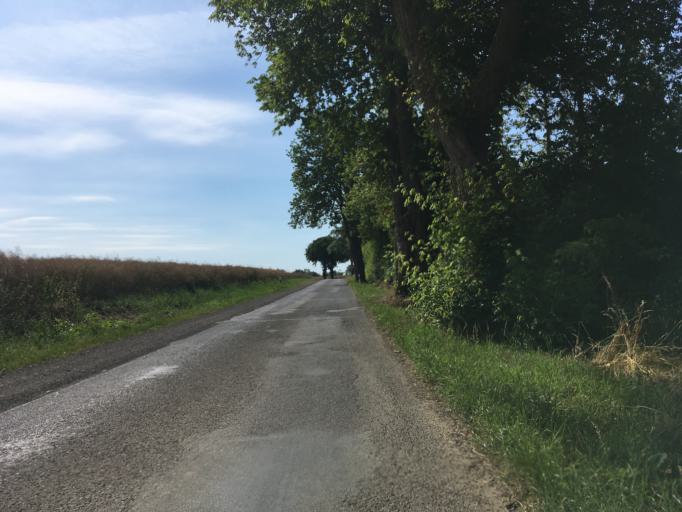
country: DE
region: Brandenburg
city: Gramzow
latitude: 53.2892
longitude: 14.0461
